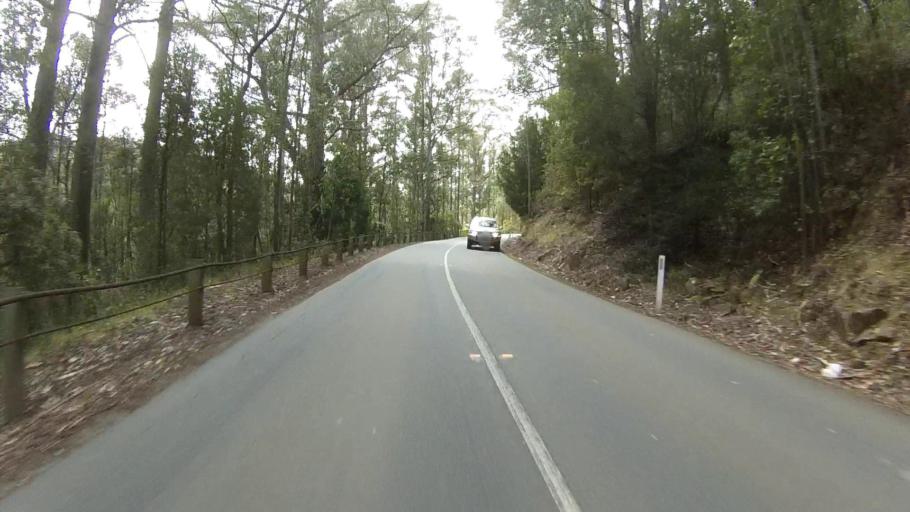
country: AU
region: Tasmania
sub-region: Kingborough
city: Kettering
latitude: -43.1273
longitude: 147.1804
